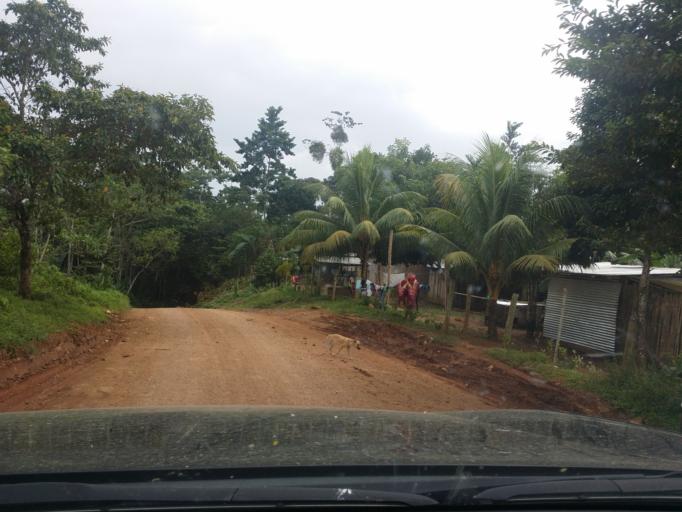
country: CR
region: Alajuela
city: Los Chiles
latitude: 11.0490
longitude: -84.4754
